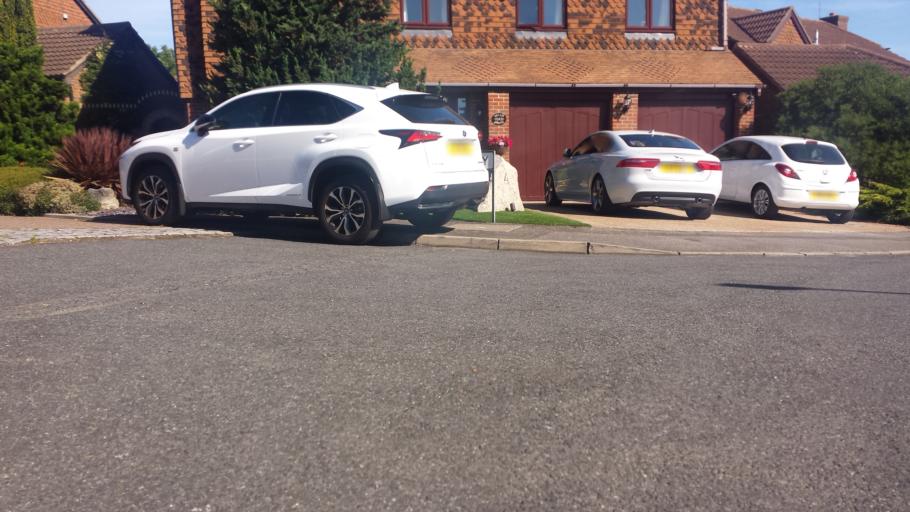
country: GB
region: England
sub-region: Kent
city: Swanley
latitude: 51.4069
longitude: 0.1610
